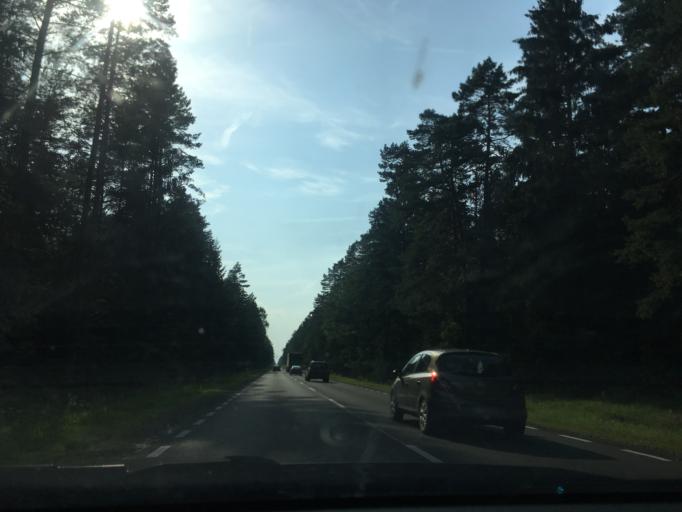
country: PL
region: Podlasie
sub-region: Powiat bialostocki
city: Suprasl
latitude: 53.1256
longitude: 23.3903
